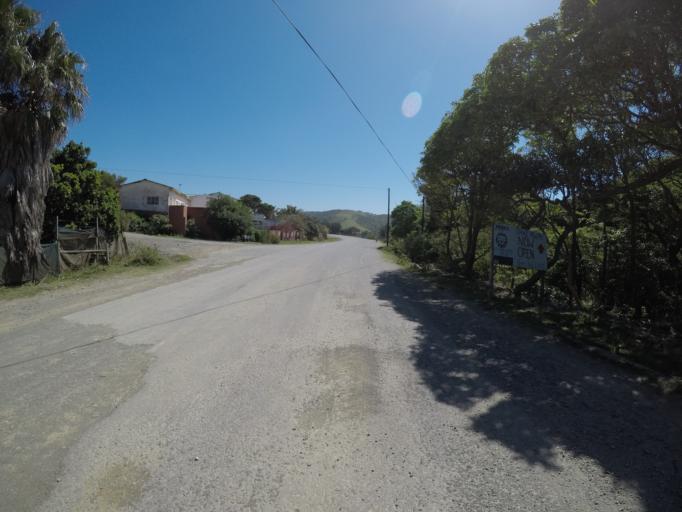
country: ZA
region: Eastern Cape
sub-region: OR Tambo District Municipality
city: Libode
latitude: -31.9862
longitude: 29.1482
